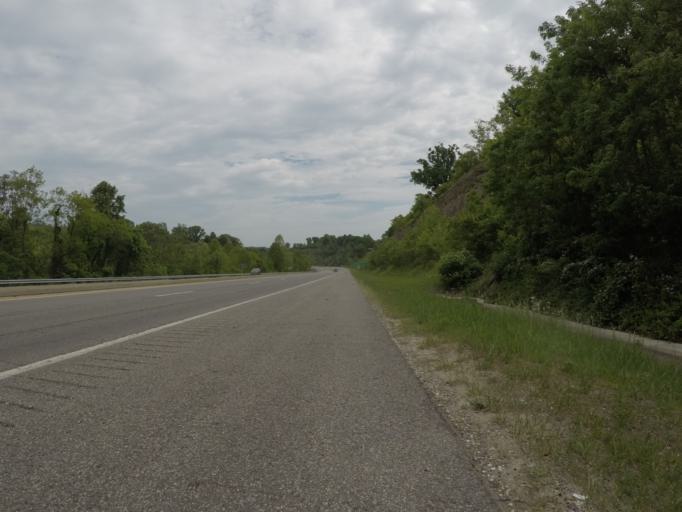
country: US
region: West Virginia
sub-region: Wayne County
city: Kenova
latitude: 38.3833
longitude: -82.5779
